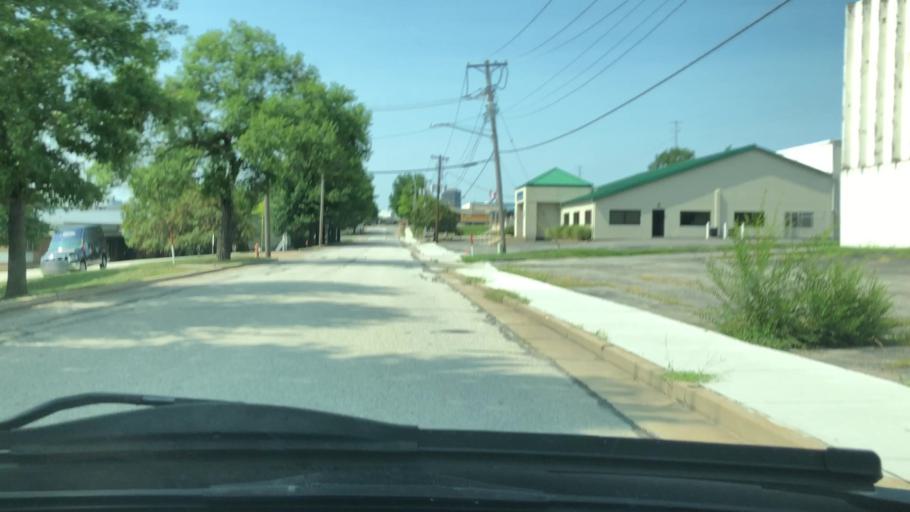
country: US
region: Missouri
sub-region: Saint Louis County
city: Brentwood
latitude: 38.6197
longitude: -90.3362
